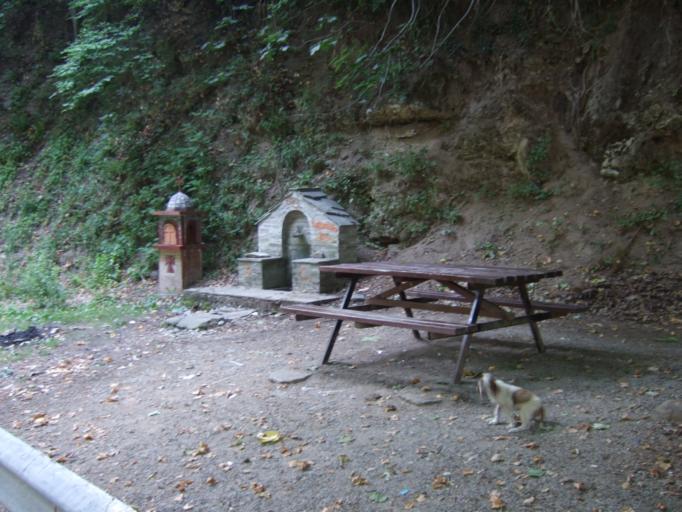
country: GR
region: Central Macedonia
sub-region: Nomos Imathias
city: Veroia
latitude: 40.4581
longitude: 22.2369
